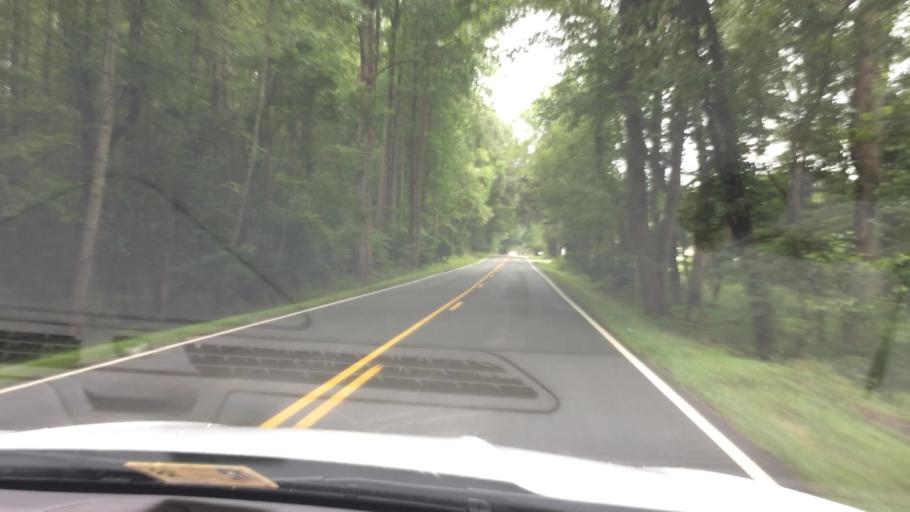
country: US
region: Virginia
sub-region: New Kent County
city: New Kent
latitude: 37.4616
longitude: -77.0351
